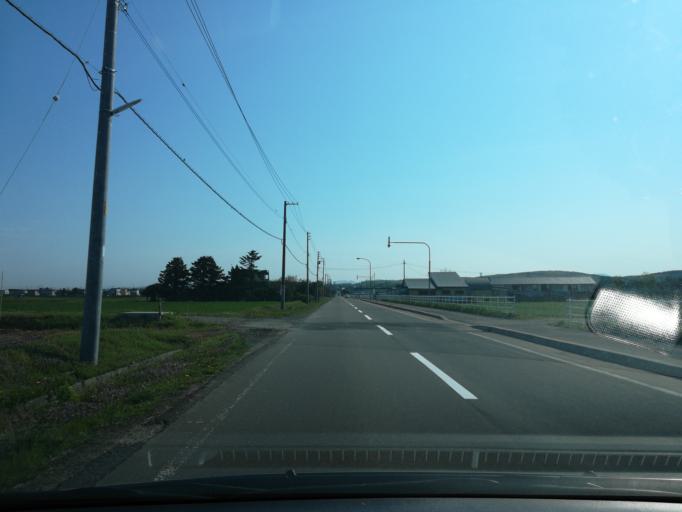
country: JP
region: Hokkaido
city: Iwamizawa
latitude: 43.1690
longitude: 141.7512
